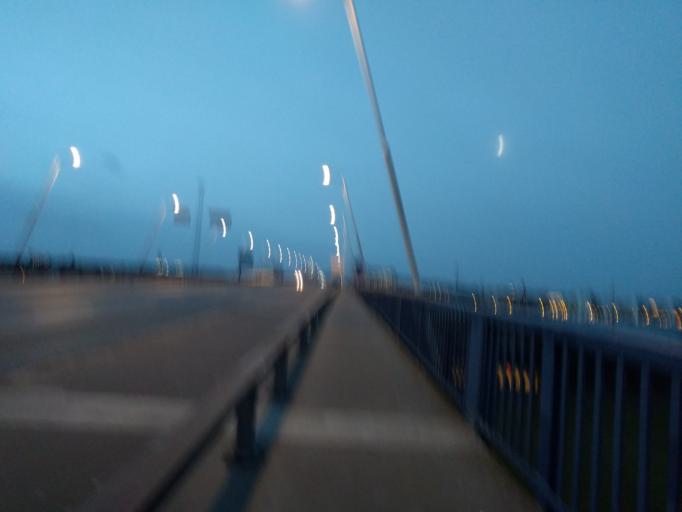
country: DK
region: North Denmark
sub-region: Alborg Kommune
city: Aalborg
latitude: 57.0571
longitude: 9.9221
